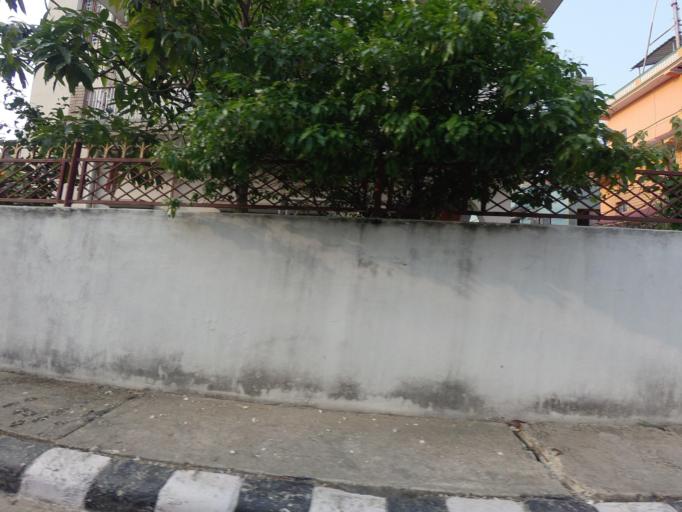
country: NP
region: Western Region
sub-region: Lumbini Zone
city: Bhairahawa
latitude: 27.5109
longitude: 83.4574
